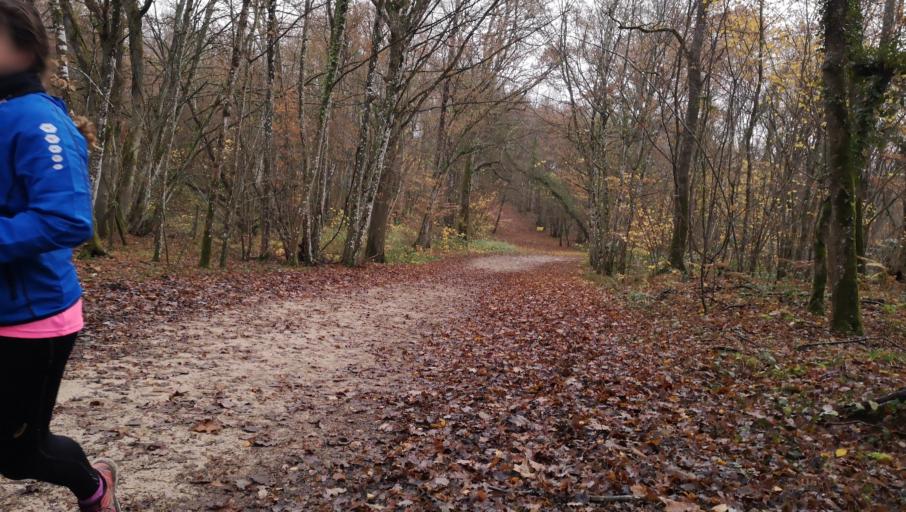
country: FR
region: Centre
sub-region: Departement du Loiret
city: Marigny-les-Usages
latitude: 47.9437
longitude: 1.9896
